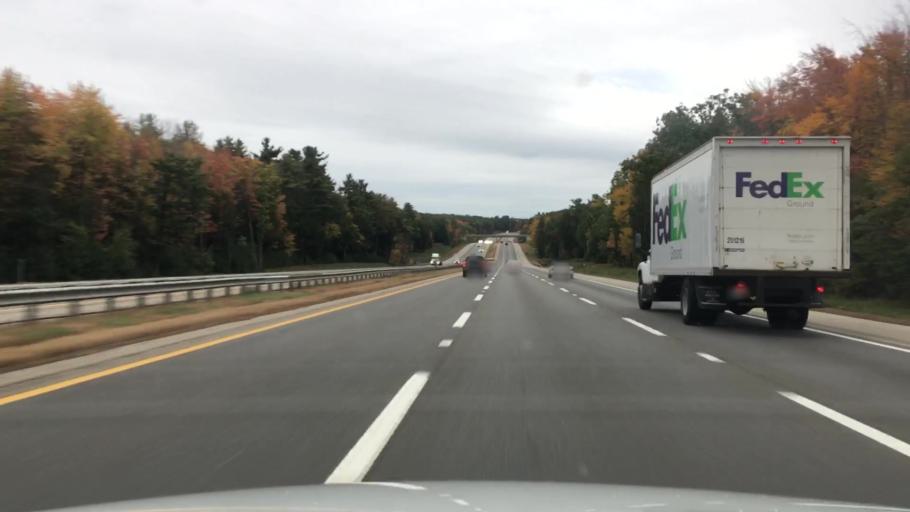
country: US
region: Maine
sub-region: York County
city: Ogunquit
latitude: 43.2702
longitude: -70.6188
